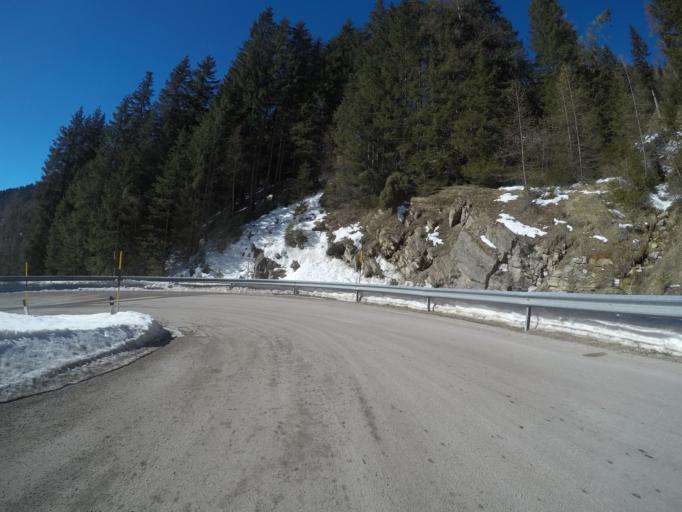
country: IT
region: Veneto
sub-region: Provincia di Belluno
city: Colle Santa Lucia
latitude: 46.4708
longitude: 12.0314
